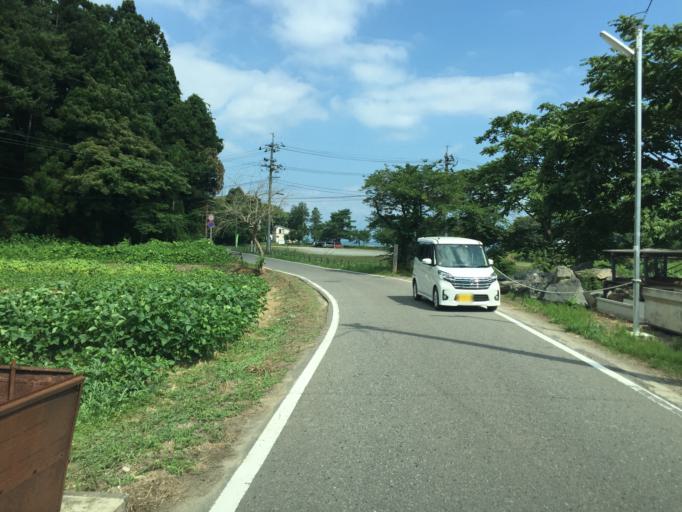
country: JP
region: Fukushima
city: Inawashiro
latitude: 37.4138
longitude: 140.1236
